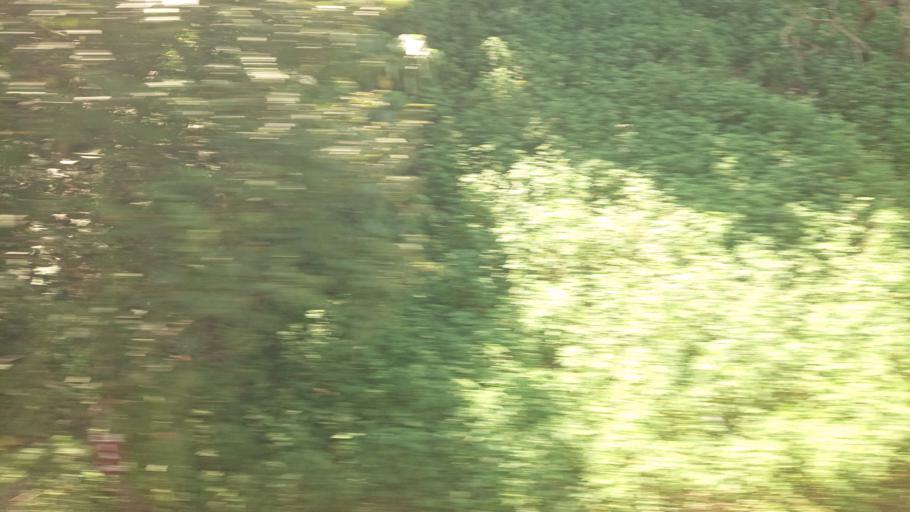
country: TW
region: Taiwan
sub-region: Nantou
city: Puli
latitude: 24.0627
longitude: 120.9494
